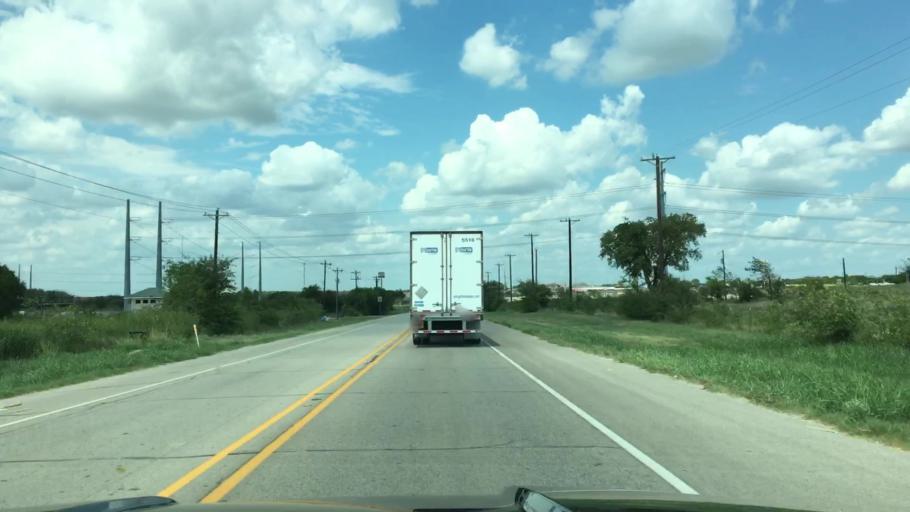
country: US
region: Texas
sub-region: Tarrant County
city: Pecan Acres
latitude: 32.9612
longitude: -97.4208
